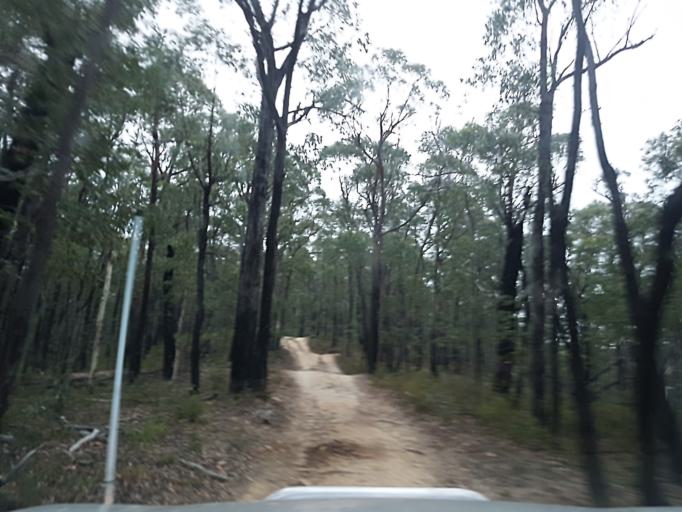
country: AU
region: New South Wales
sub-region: Snowy River
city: Jindabyne
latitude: -36.8548
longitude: 148.2303
